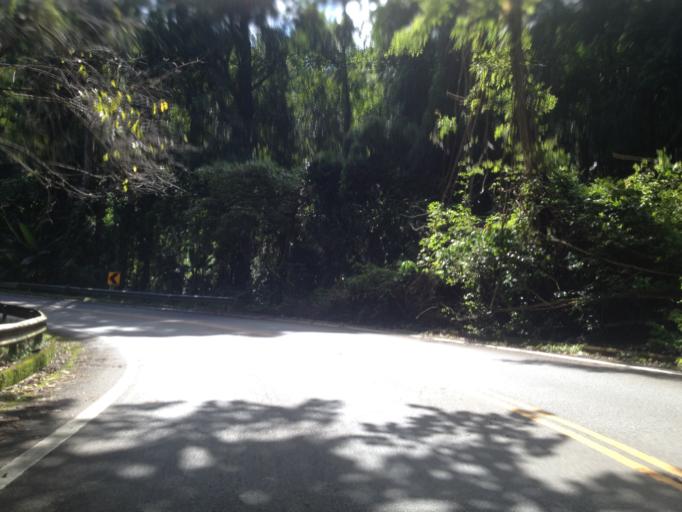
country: TH
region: Chiang Mai
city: Chiang Mai
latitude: 18.8026
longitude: 98.9089
